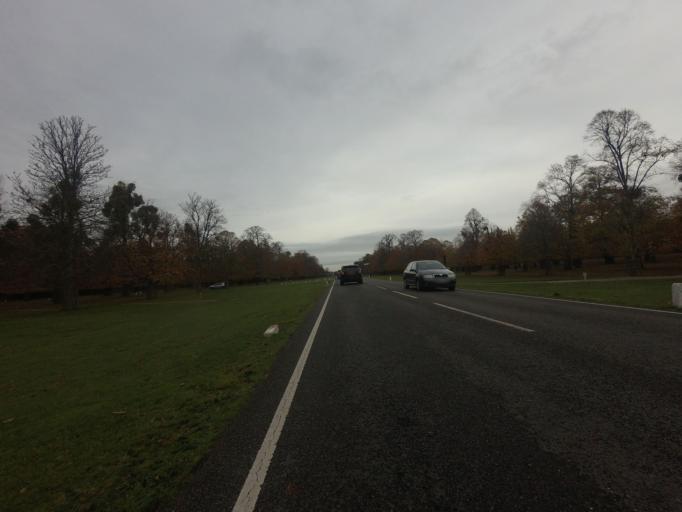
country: GB
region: England
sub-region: Greater London
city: Teddington
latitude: 51.4166
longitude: -0.3345
